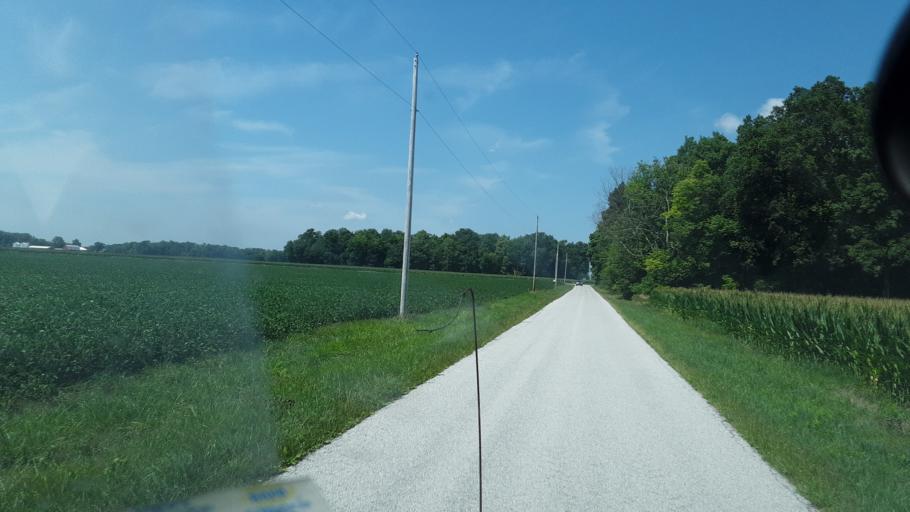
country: US
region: Ohio
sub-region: Hancock County
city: Findlay
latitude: 40.9923
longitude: -83.5322
